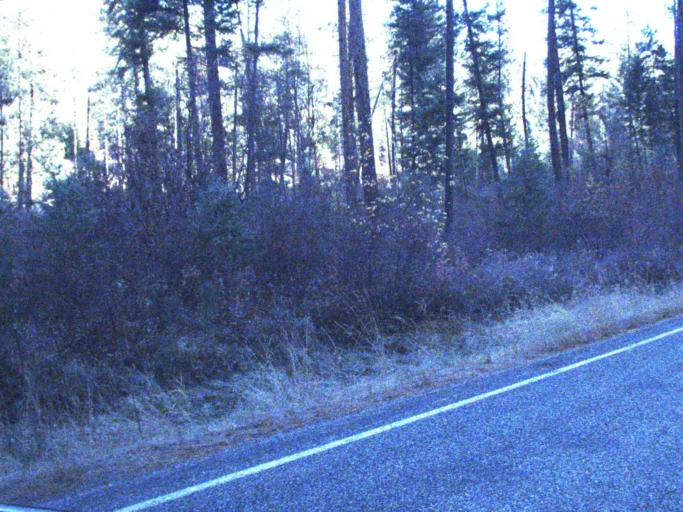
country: US
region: Washington
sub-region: Ferry County
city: Republic
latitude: 48.3938
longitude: -118.7429
